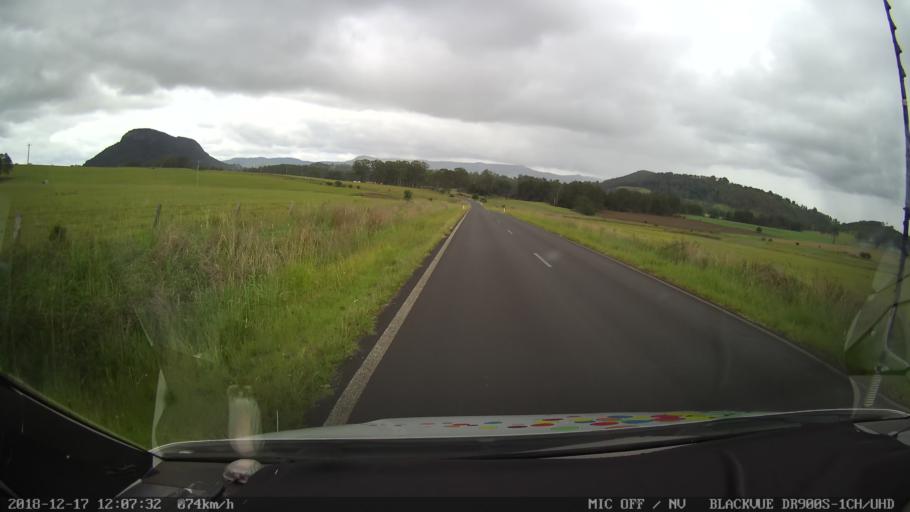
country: AU
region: New South Wales
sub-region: Kyogle
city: Kyogle
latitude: -28.4743
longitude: 152.5645
